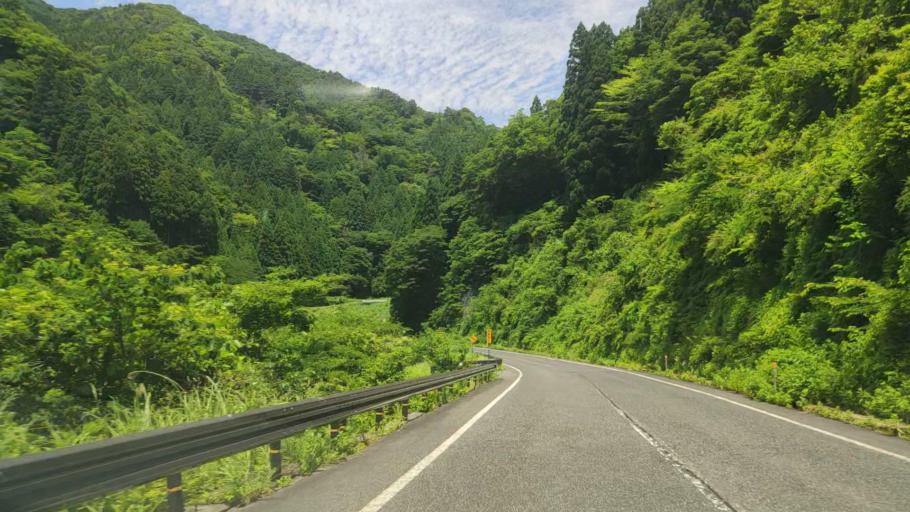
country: JP
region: Tottori
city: Tottori
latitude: 35.3480
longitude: 134.4509
